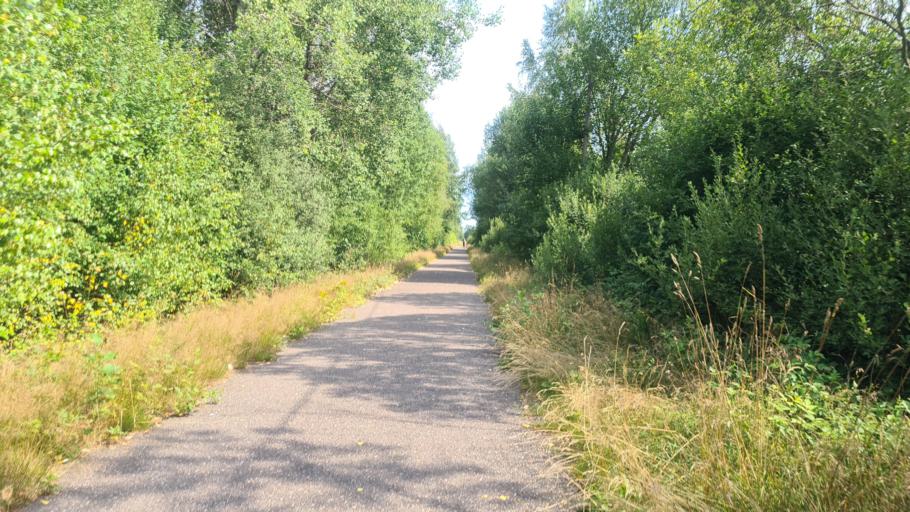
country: SE
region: Kronoberg
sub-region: Ljungby Kommun
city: Ljungby
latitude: 56.8489
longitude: 13.9670
